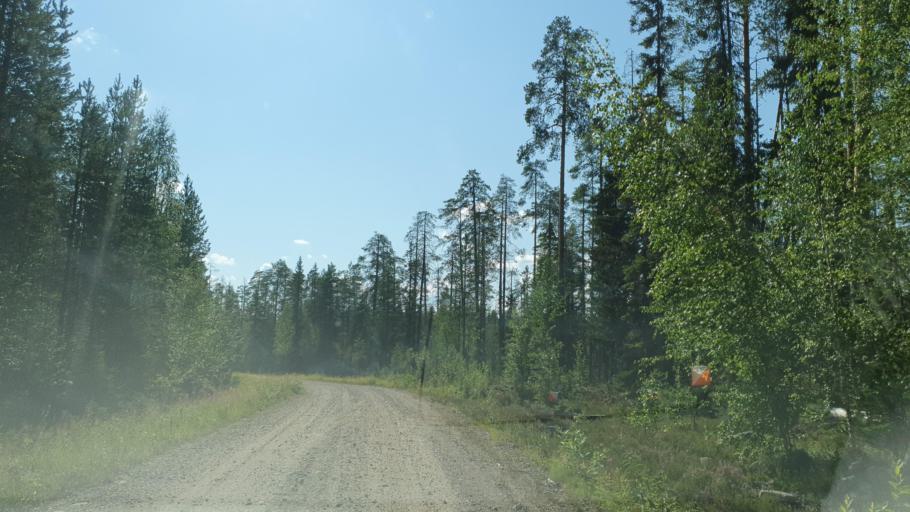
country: FI
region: Kainuu
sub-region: Kehys-Kainuu
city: Kuhmo
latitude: 63.9620
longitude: 29.5365
